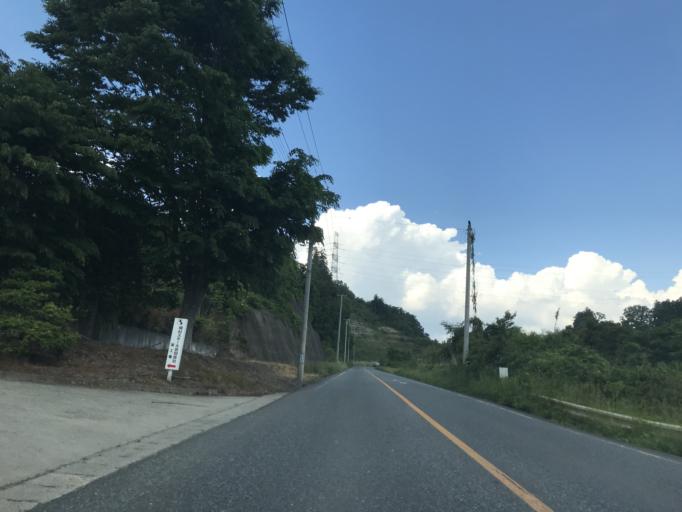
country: JP
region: Miyagi
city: Wakuya
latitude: 38.5656
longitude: 141.1376
